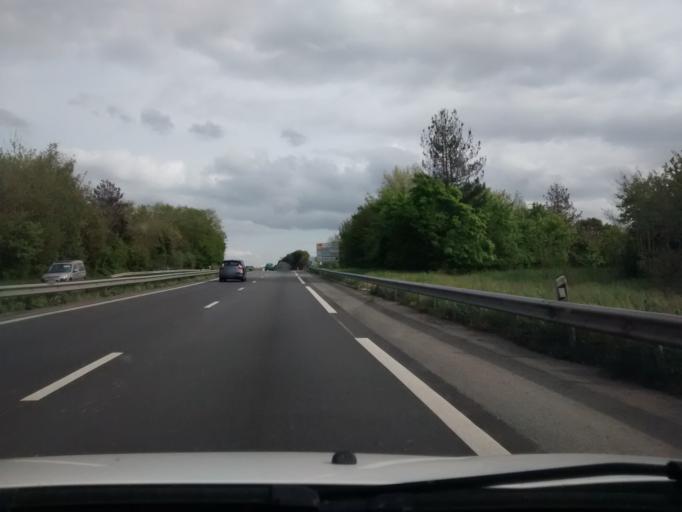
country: FR
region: Brittany
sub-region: Departement d'Ille-et-Vilaine
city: Saint-Pere
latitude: 48.5701
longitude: -1.9319
